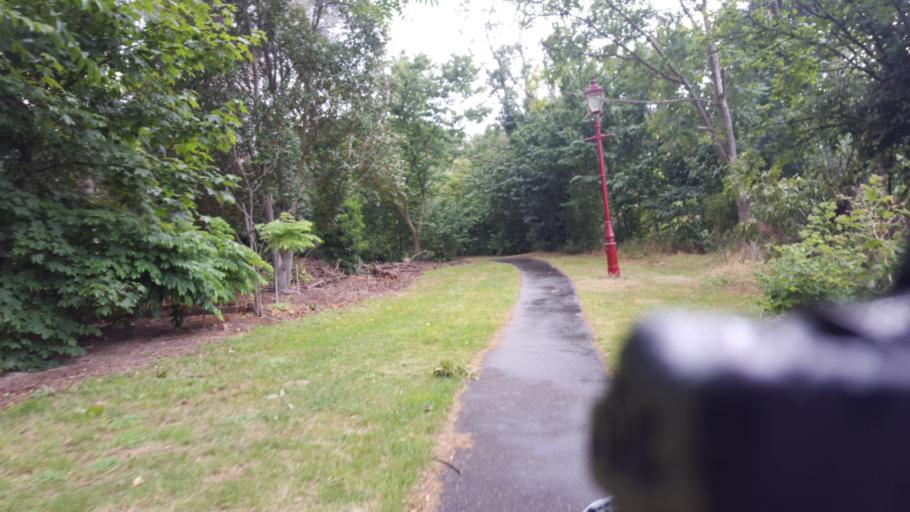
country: NZ
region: Otago
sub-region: Queenstown-Lakes District
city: Wanaka
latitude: -45.1849
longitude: 169.3153
